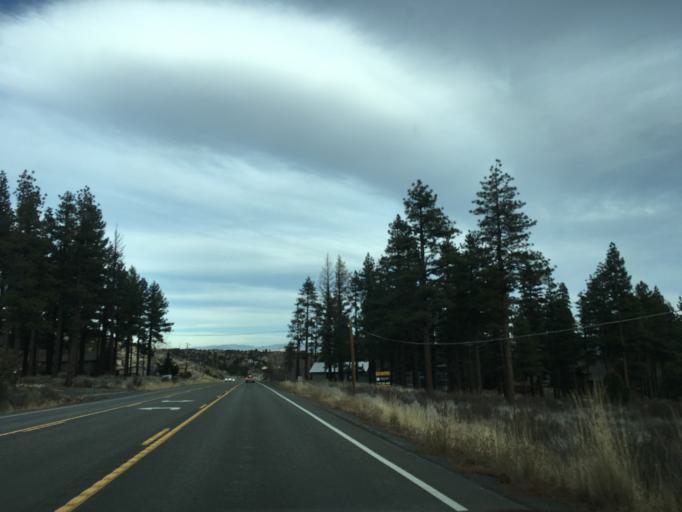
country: US
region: Nevada
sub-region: Washoe County
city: Reno
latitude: 39.3716
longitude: -119.8449
